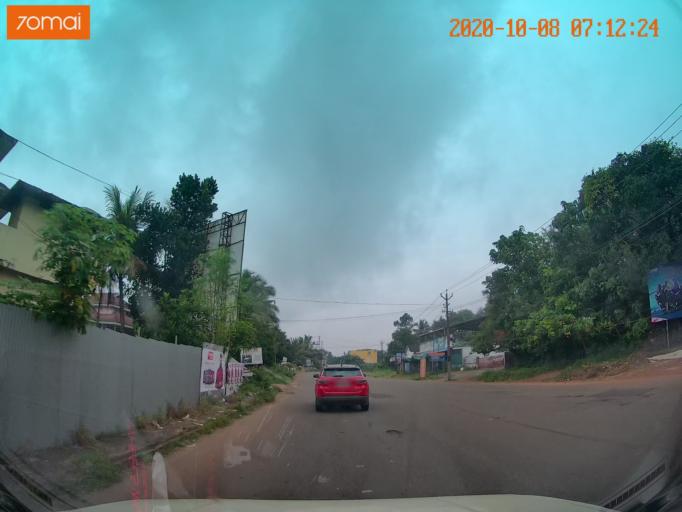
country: IN
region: Kerala
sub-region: Malappuram
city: Ponnani
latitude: 10.8030
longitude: 76.0082
